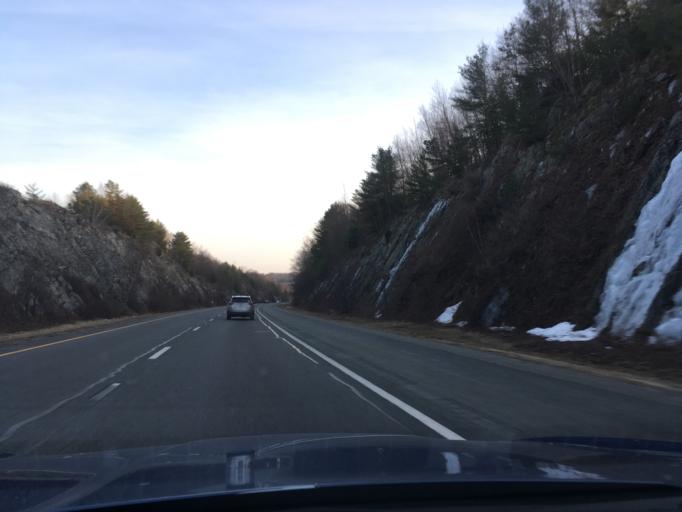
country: US
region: Rhode Island
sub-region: Providence County
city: Cranston
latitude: 41.7715
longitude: -71.4871
